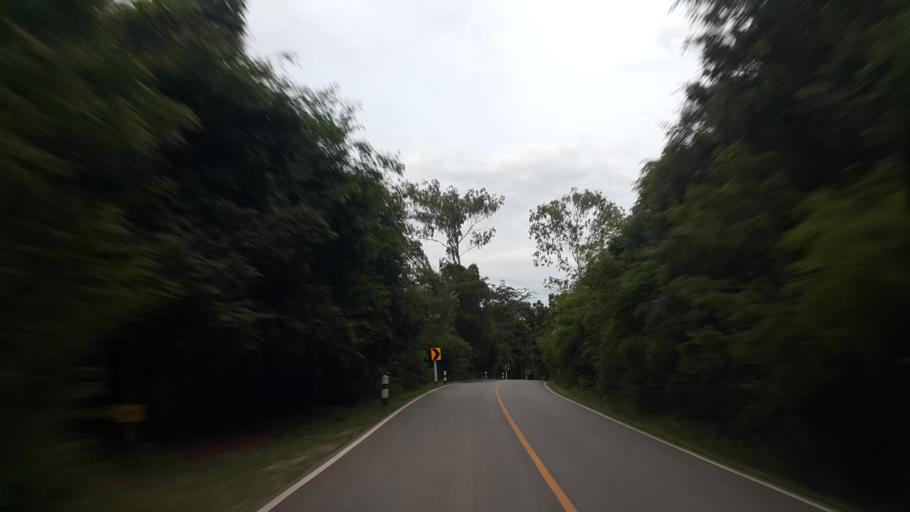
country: TH
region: Loei
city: Na Haeo
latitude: 17.5302
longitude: 101.1979
